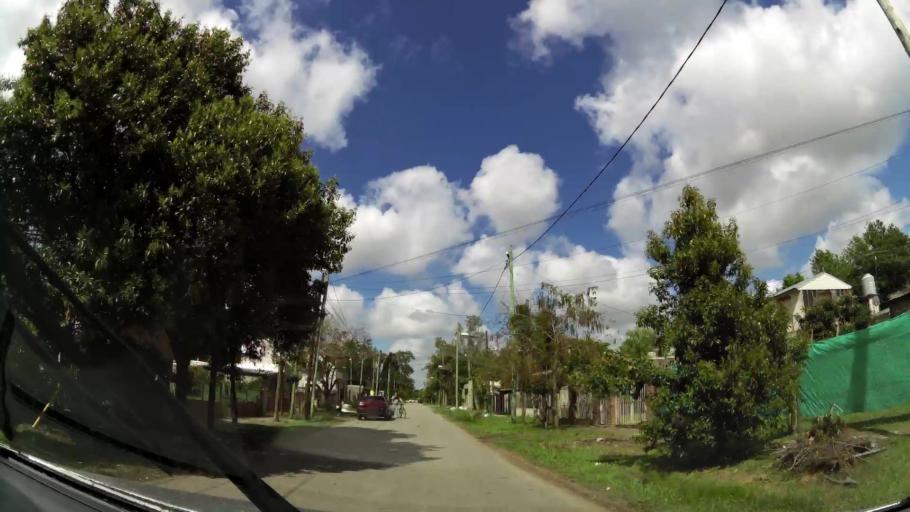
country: AR
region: Buenos Aires
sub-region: Partido de Quilmes
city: Quilmes
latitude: -34.8331
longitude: -58.1739
